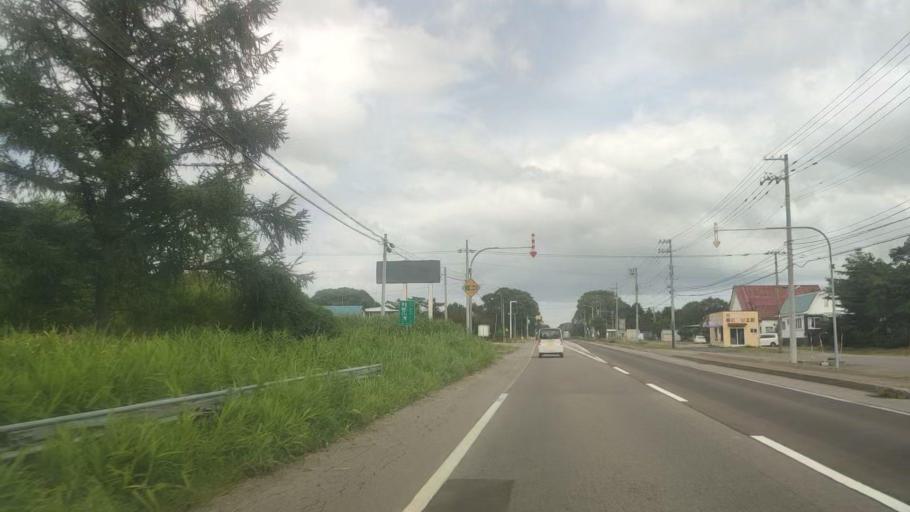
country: JP
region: Hokkaido
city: Nanae
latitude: 42.0349
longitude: 140.6078
